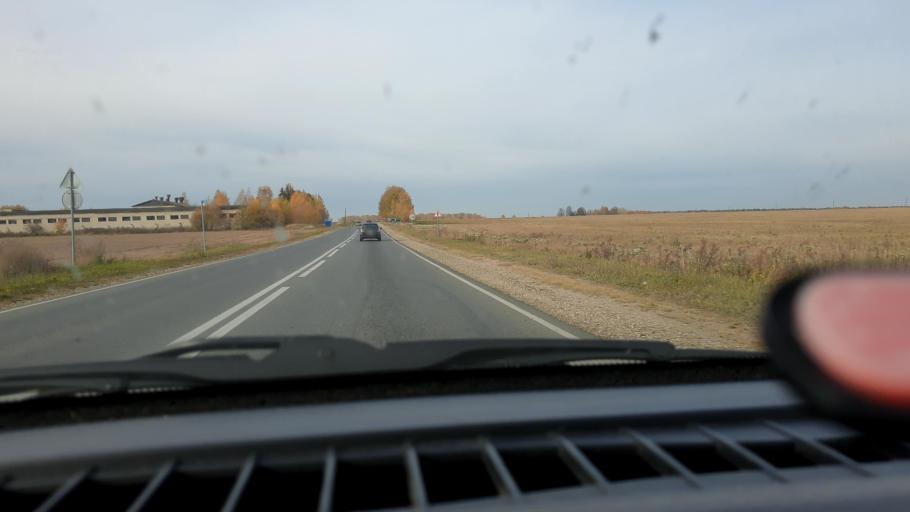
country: RU
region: Nizjnij Novgorod
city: Gorodets
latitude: 56.6229
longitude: 43.5508
